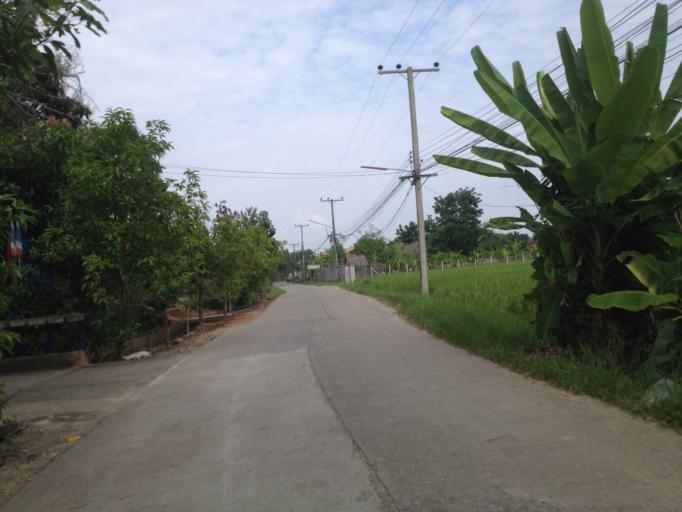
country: TH
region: Chiang Mai
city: Hang Dong
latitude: 18.6716
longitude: 98.8993
